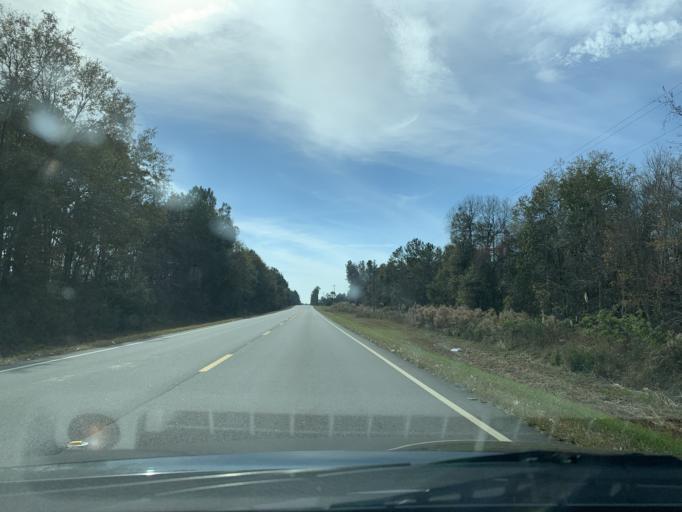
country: US
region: Georgia
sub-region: Turner County
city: Ashburn
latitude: 31.7406
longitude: -83.5713
